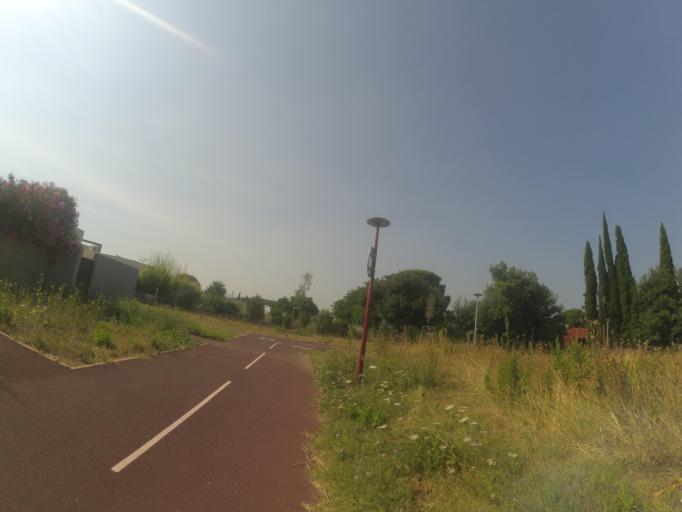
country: FR
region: Languedoc-Roussillon
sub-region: Departement des Pyrenees-Orientales
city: Toulouges
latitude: 42.6656
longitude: 2.8227
